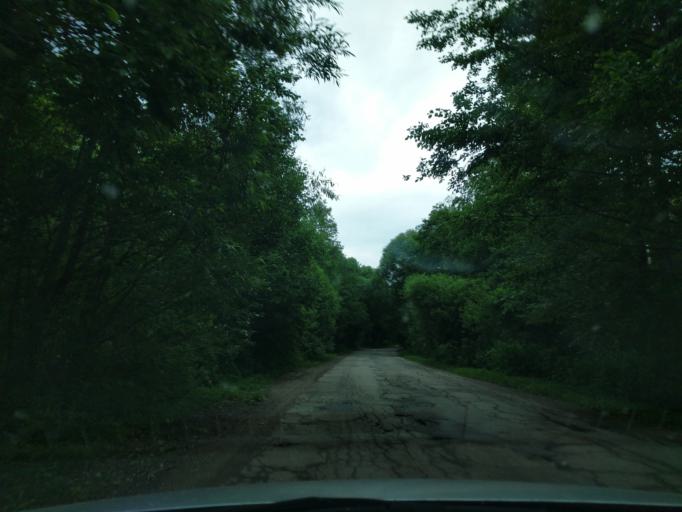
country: RU
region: Kaluga
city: Nikola-Lenivets
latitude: 54.7677
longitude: 35.7091
